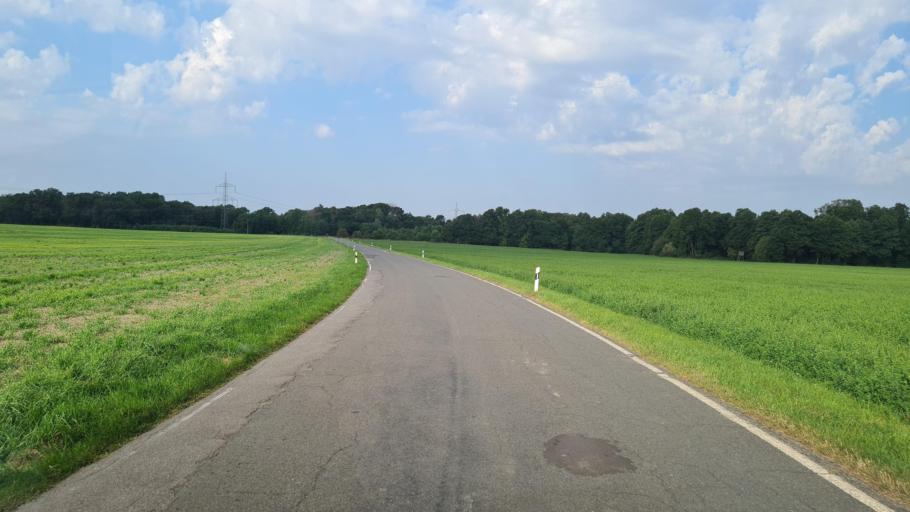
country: DE
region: Brandenburg
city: Drebkau
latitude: 51.6738
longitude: 14.2186
